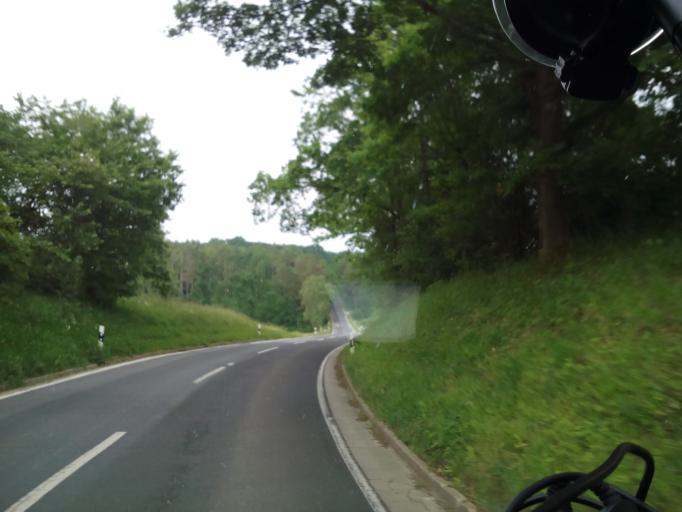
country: DE
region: Bavaria
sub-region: Regierungsbezirk Unterfranken
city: Hendungen
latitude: 50.3975
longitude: 10.3677
